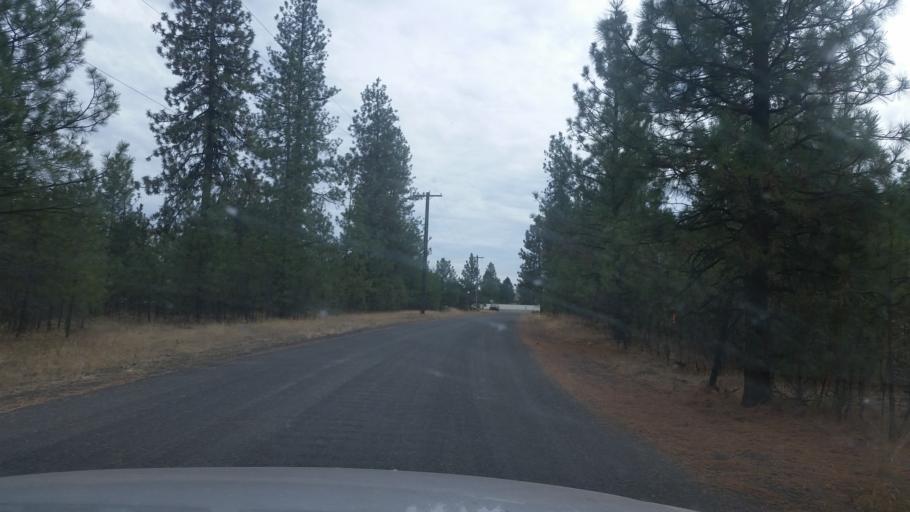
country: US
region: Washington
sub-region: Spokane County
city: Cheney
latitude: 47.5157
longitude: -117.5655
